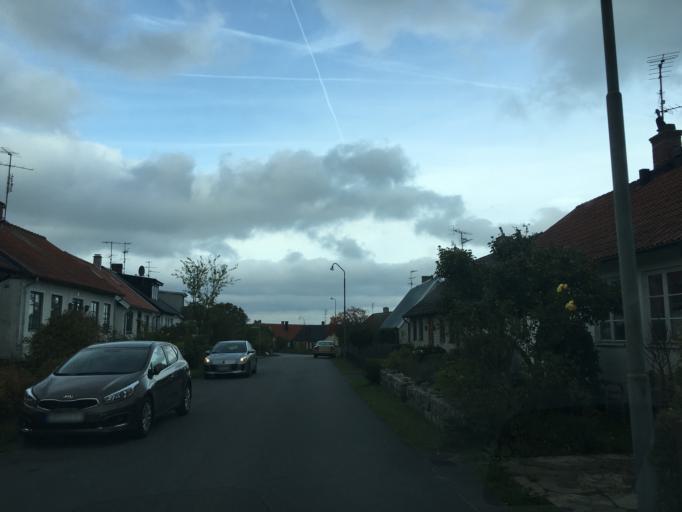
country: SE
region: Skane
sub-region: Simrishamns Kommun
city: Simrishamn
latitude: 55.5913
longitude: 14.3173
